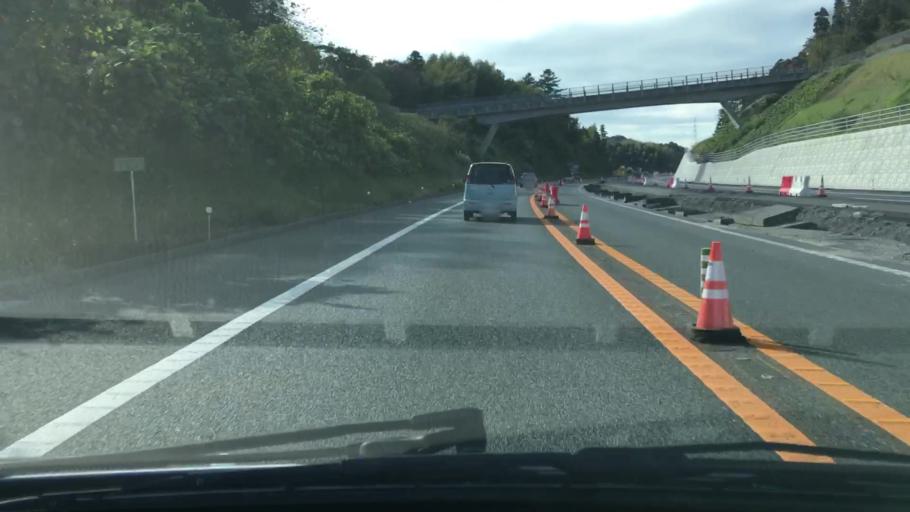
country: JP
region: Chiba
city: Kimitsu
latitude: 35.3013
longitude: 139.9399
